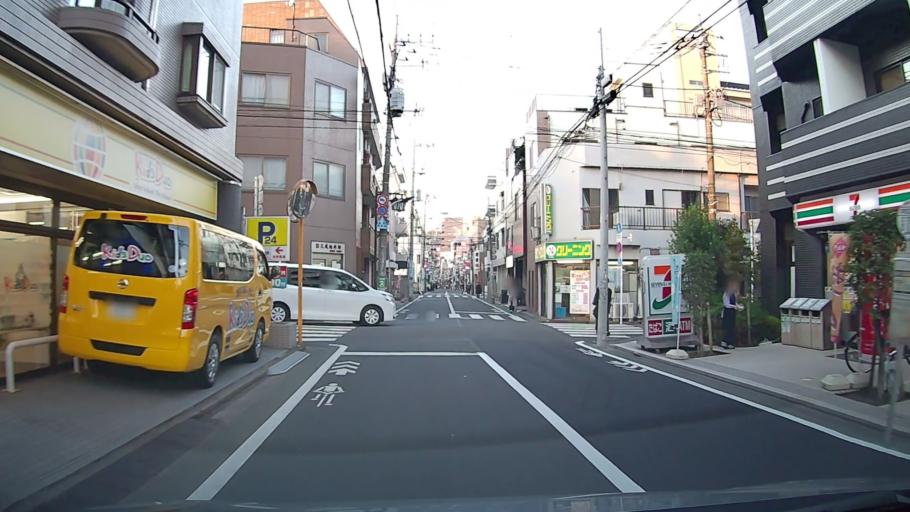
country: JP
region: Saitama
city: Wako
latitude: 35.7334
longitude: 139.6389
